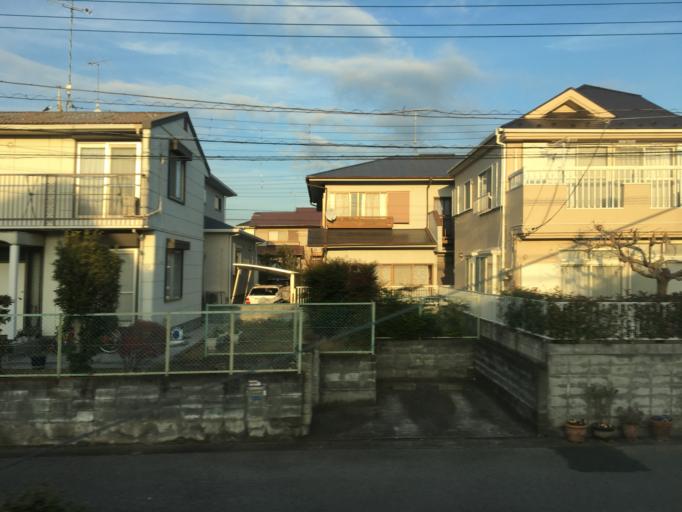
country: JP
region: Saitama
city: Fukiage-fujimi
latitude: 36.0828
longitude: 139.4797
